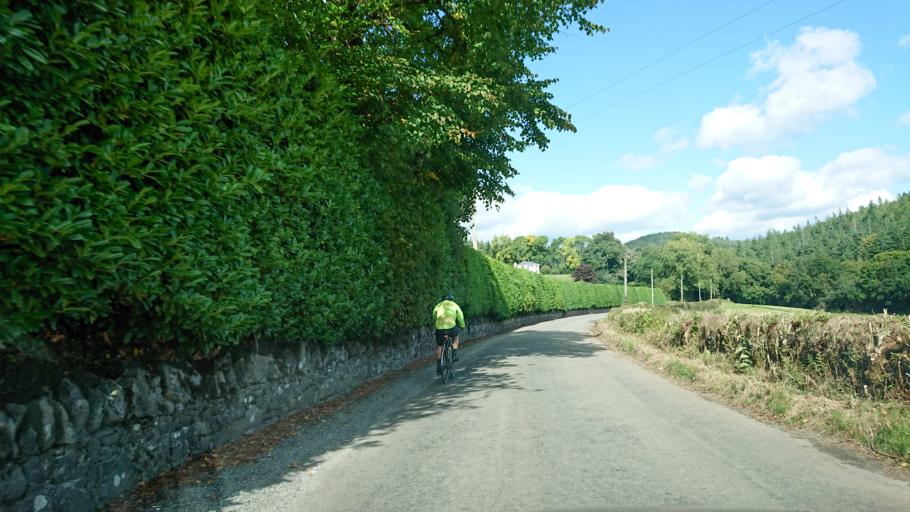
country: IE
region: Munster
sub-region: Waterford
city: Dungarvan
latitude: 52.1231
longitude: -7.6894
